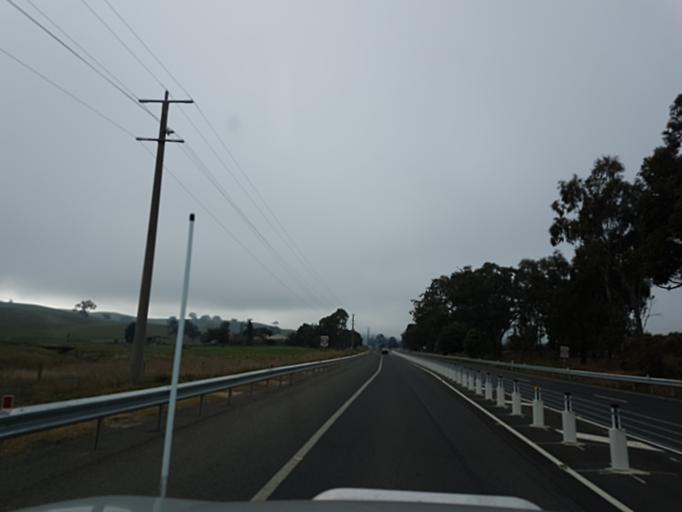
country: AU
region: Victoria
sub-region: Murrindindi
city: Alexandra
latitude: -37.2058
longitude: 145.4600
